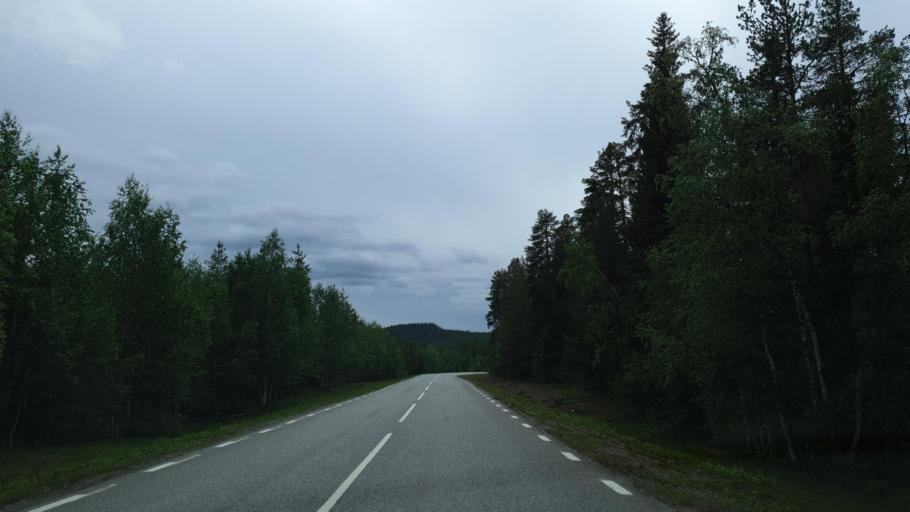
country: SE
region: Vaesterbotten
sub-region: Sorsele Kommun
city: Sorsele
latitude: 65.5193
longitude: 17.3845
